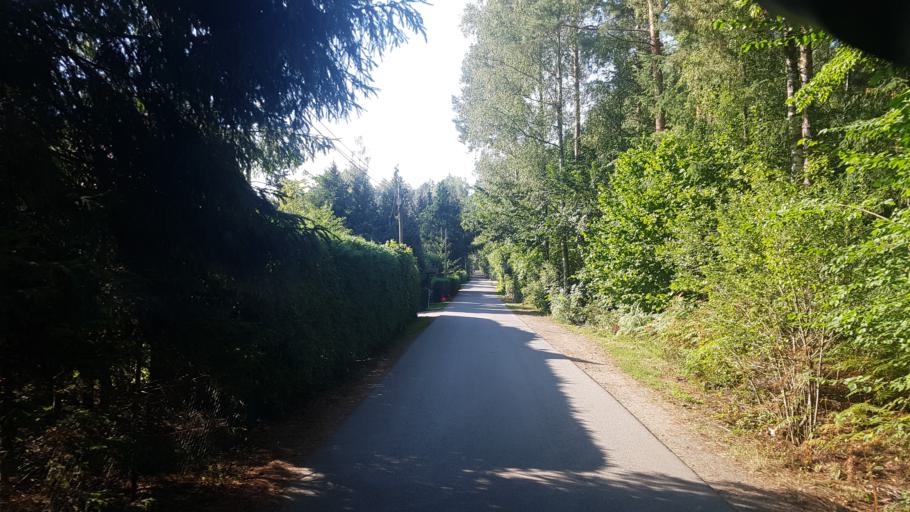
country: DE
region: Brandenburg
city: Plessa
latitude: 51.5180
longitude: 13.6508
